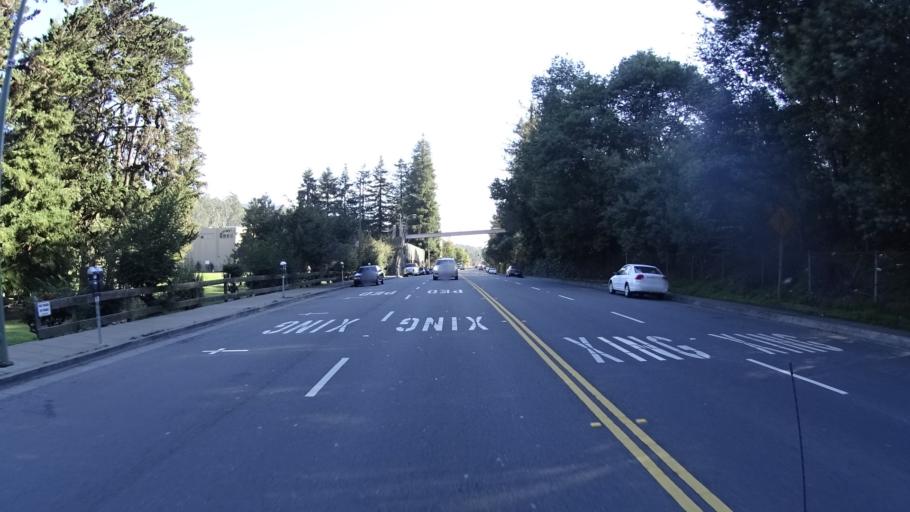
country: US
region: California
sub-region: Alameda County
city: Piedmont
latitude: 37.8287
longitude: -122.2127
